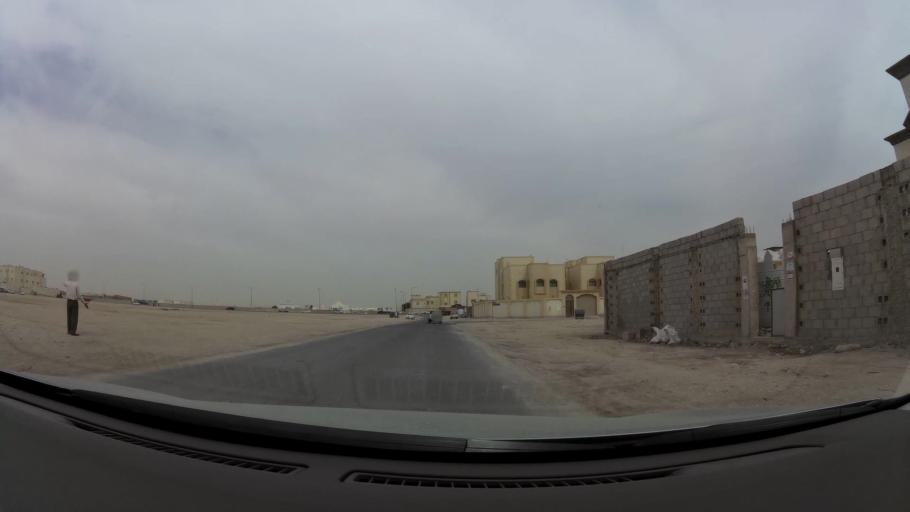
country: QA
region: Baladiyat ar Rayyan
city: Ar Rayyan
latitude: 25.2158
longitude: 51.4533
